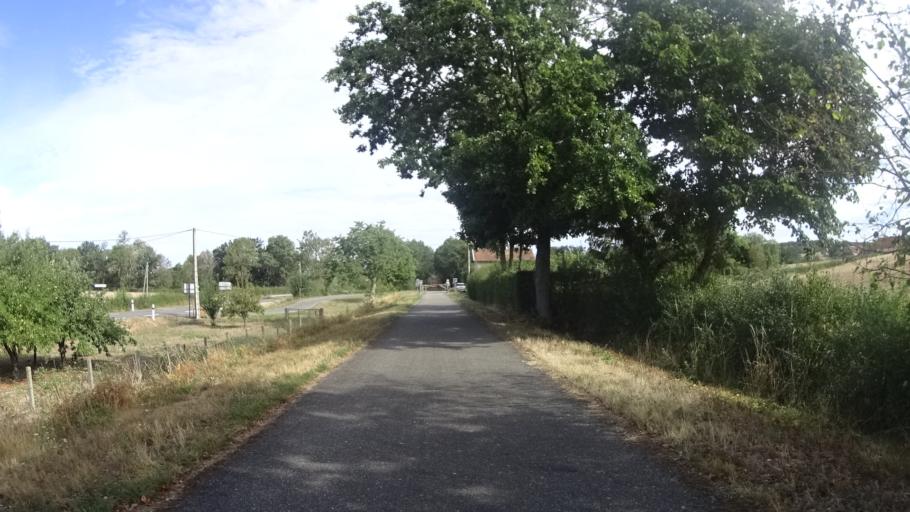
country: FR
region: Bourgogne
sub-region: Departement de Saone-et-Loire
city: Bourbon-Lancy
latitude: 46.5810
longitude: 3.7452
